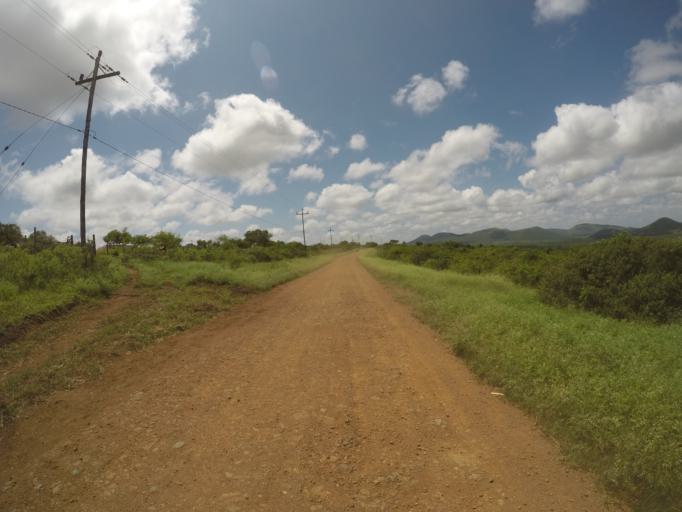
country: ZA
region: KwaZulu-Natal
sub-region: uThungulu District Municipality
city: Empangeni
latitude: -28.5866
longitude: 31.8224
